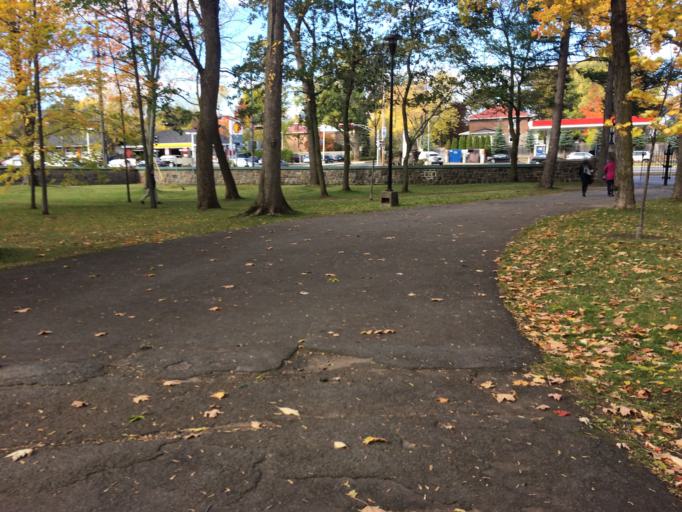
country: CA
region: Quebec
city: Quebec
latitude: 46.7891
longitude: -71.2454
